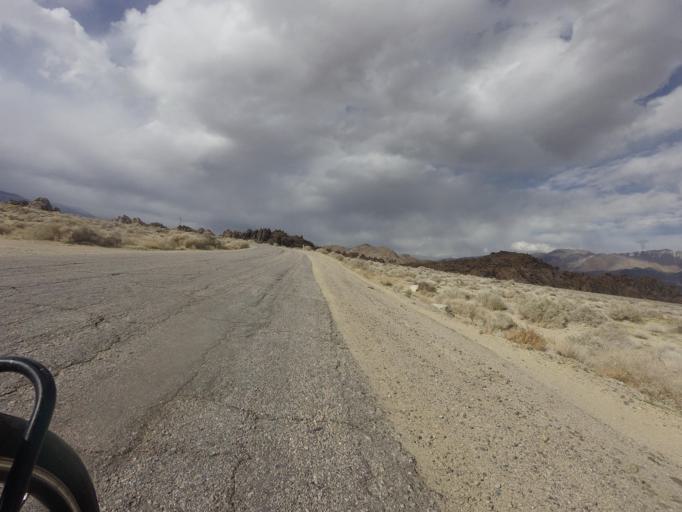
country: US
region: California
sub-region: Inyo County
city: Lone Pine
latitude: 36.5958
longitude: -118.1088
